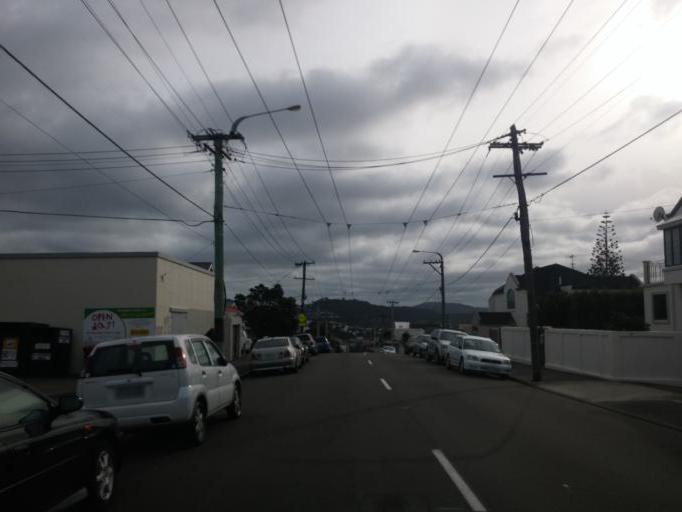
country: NZ
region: Wellington
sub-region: Wellington City
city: Brooklyn
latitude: -41.3076
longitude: 174.7668
